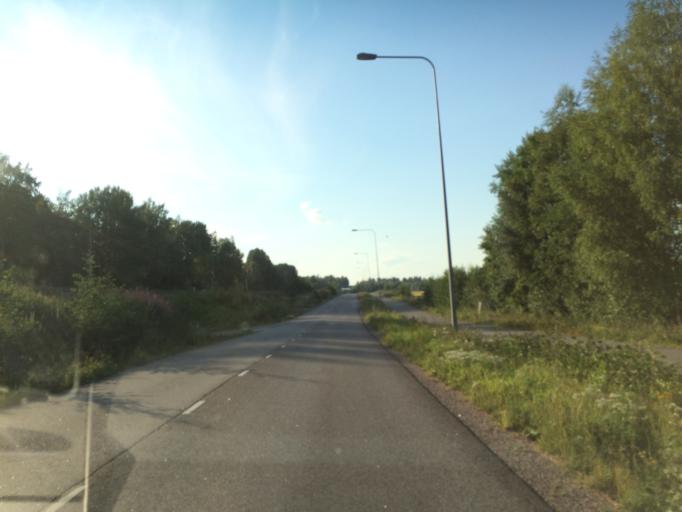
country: FI
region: Haeme
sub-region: Haemeenlinna
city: Parola
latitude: 61.0367
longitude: 24.3866
